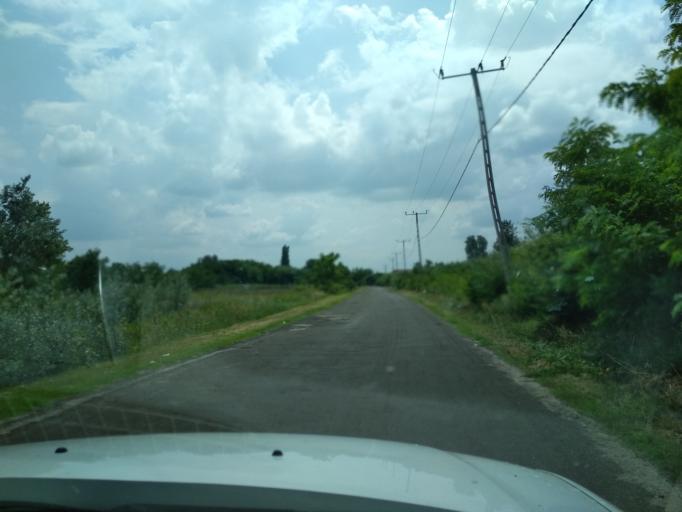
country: HU
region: Pest
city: Tapioszentmarton
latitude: 47.3777
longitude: 19.7574
